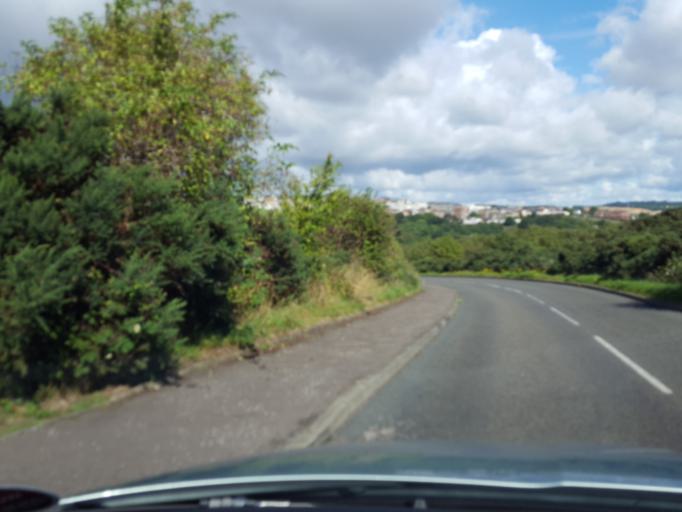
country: GB
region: Scotland
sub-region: Fife
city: Inverkeithing
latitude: 56.0205
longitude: -3.4014
